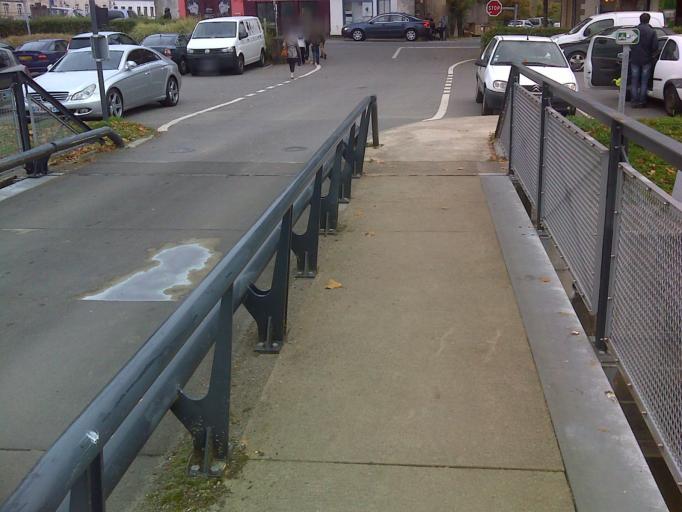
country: FR
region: Brittany
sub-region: Departement d'Ille-et-Vilaine
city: Redon
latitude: 47.6477
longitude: -2.0836
